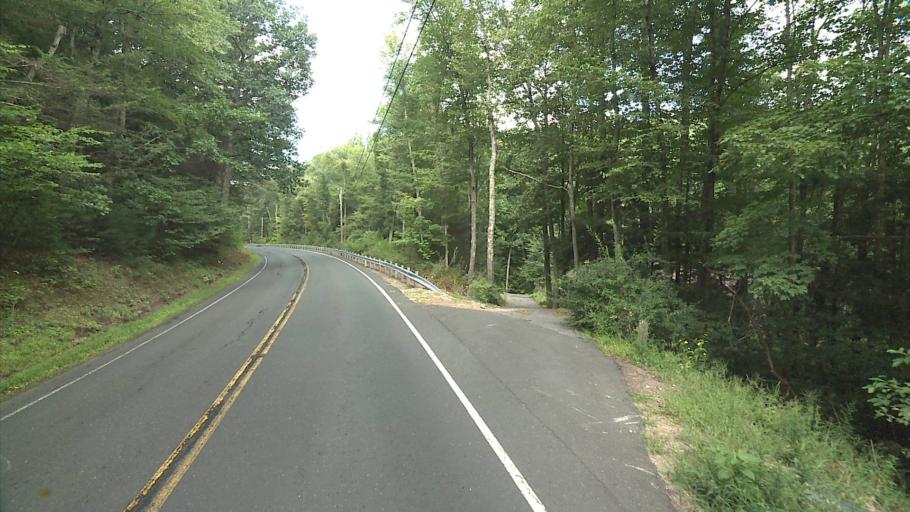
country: US
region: Connecticut
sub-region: Hartford County
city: North Granby
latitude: 42.0192
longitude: -72.8511
